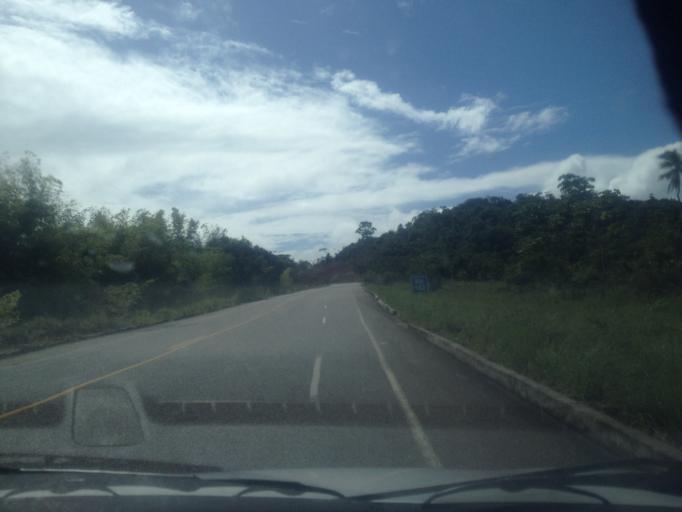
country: BR
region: Bahia
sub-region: Conde
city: Conde
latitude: -11.7681
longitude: -37.5910
